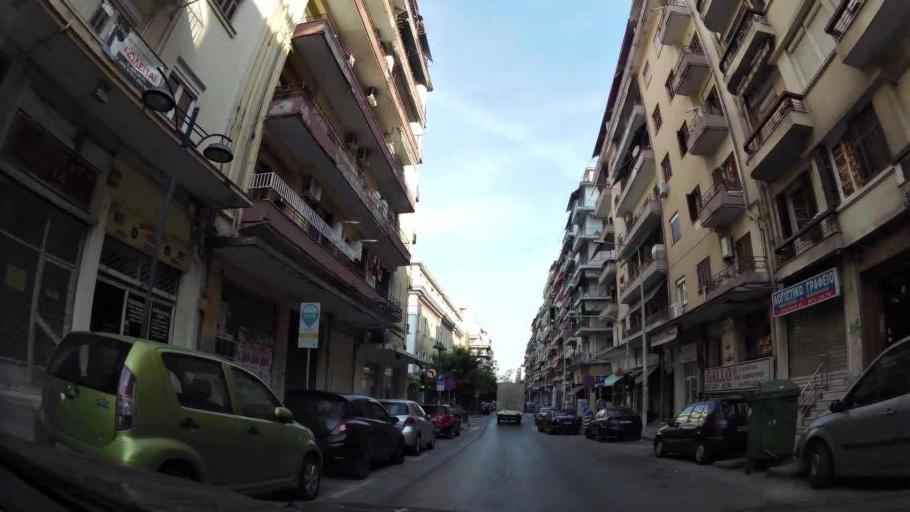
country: GR
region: Central Macedonia
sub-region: Nomos Thessalonikis
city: Sykies
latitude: 40.6408
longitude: 22.9456
